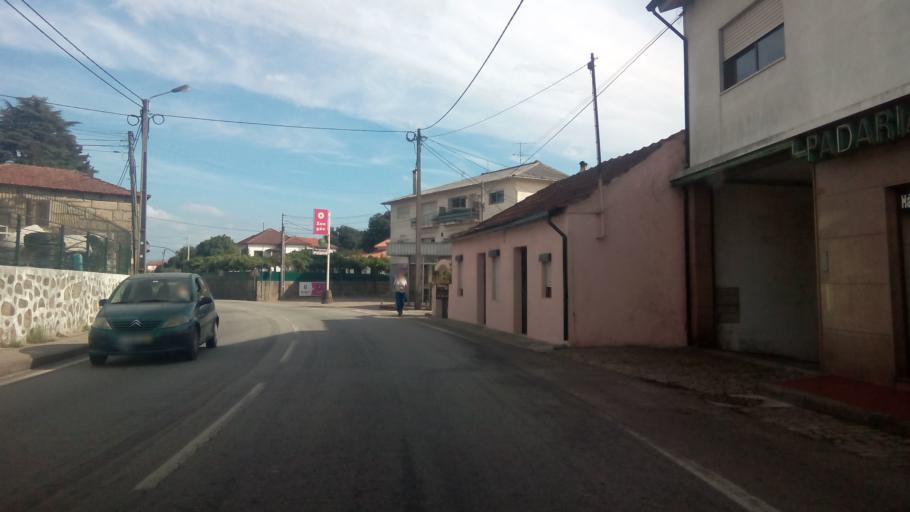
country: PT
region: Porto
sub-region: Paredes
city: Baltar
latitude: 41.1901
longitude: -8.3835
